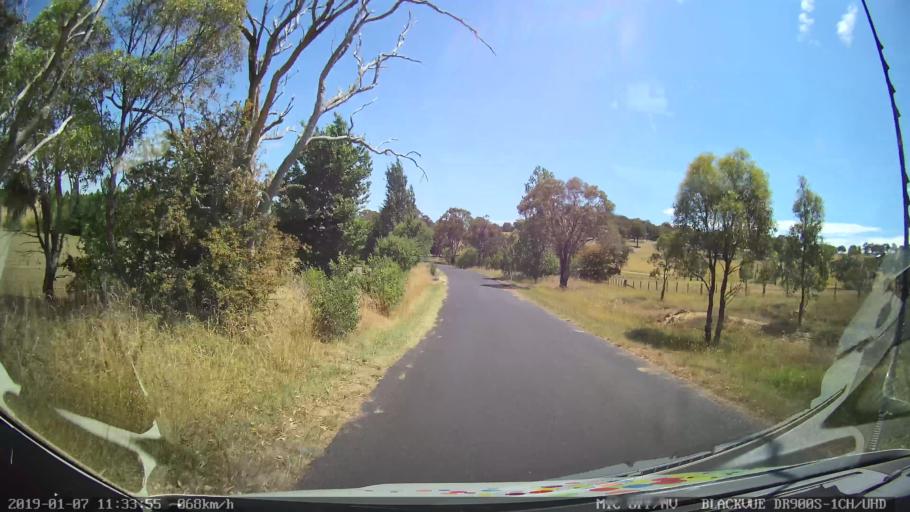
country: AU
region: New South Wales
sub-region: Armidale Dumaresq
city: Armidale
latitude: -30.3949
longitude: 151.5606
